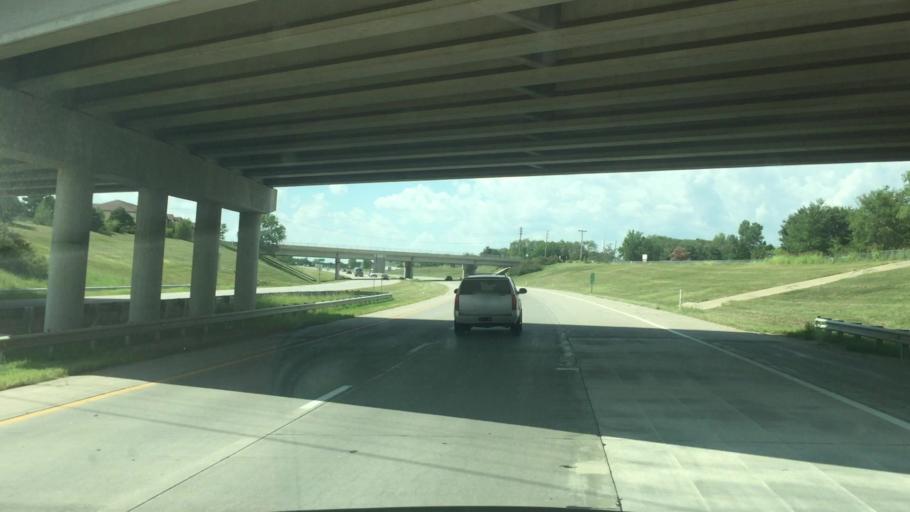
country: US
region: Kansas
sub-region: Butler County
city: Andover
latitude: 37.6939
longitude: -97.1875
